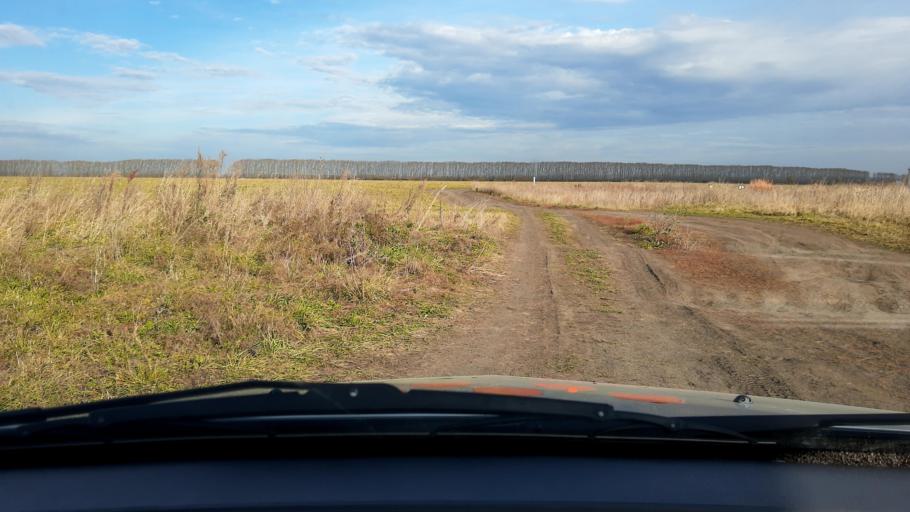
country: RU
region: Bashkortostan
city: Asanovo
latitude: 54.8093
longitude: 55.6114
